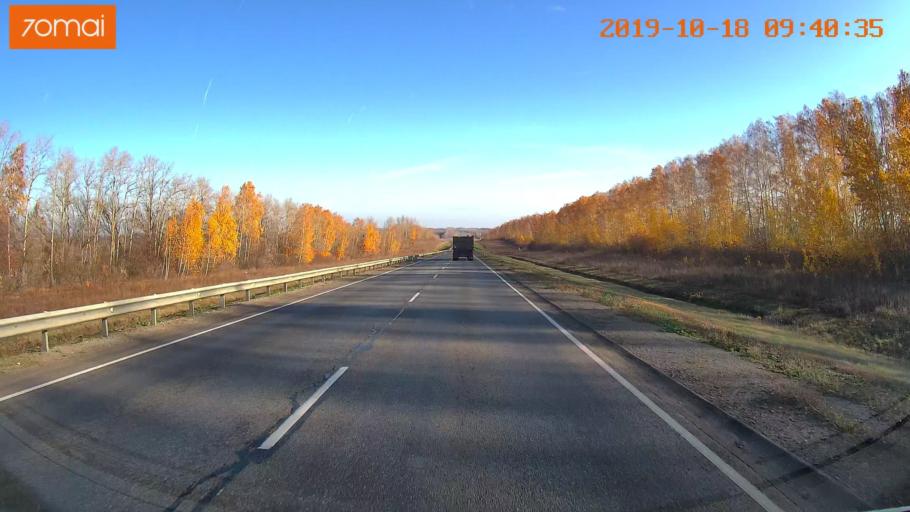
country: RU
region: Tula
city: Kazachka
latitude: 53.2656
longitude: 38.1501
